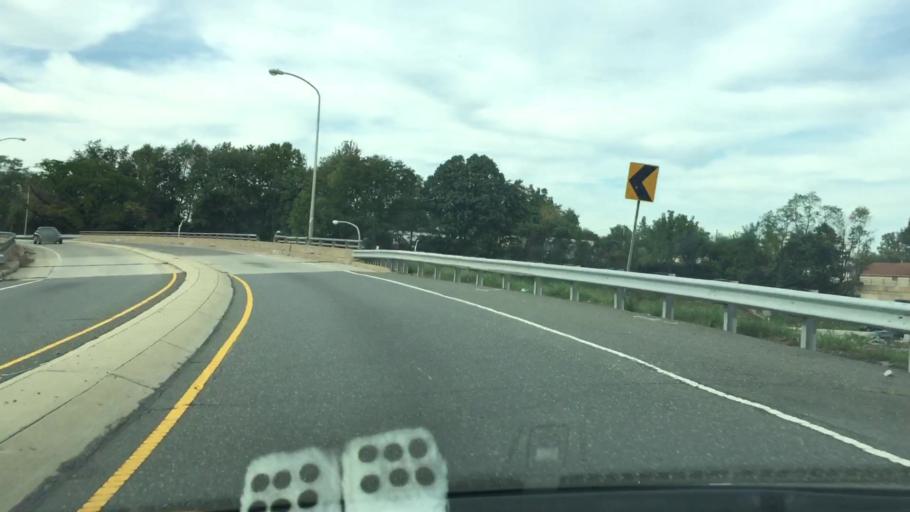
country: US
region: New Jersey
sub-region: Burlington County
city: Riverton
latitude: 40.0474
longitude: -74.9991
